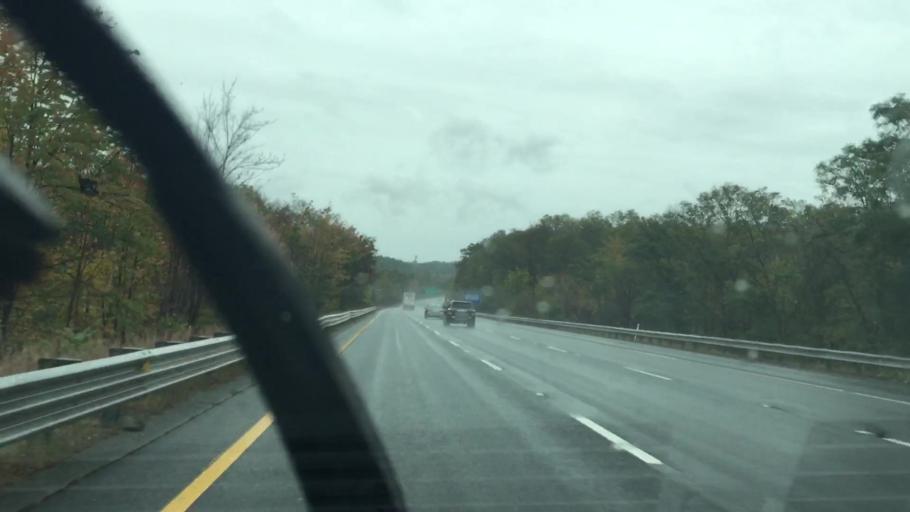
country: US
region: Massachusetts
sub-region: Essex County
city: Merrimac
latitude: 42.8237
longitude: -71.0104
